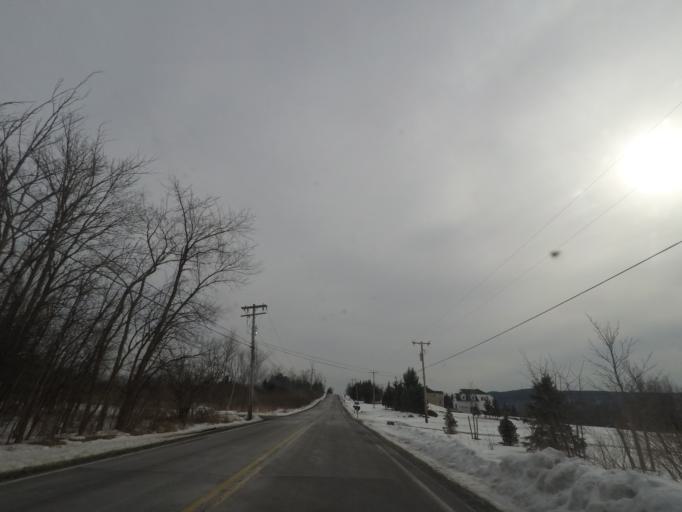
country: US
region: New York
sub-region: Albany County
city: Altamont
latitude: 42.6801
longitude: -73.9825
